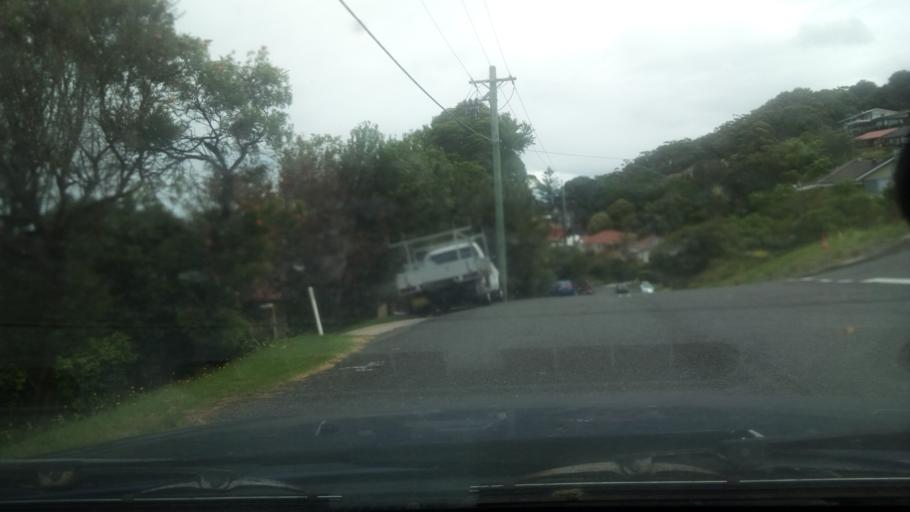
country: AU
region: New South Wales
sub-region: Wollongong
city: Wollongong
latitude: -34.4302
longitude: 150.8825
